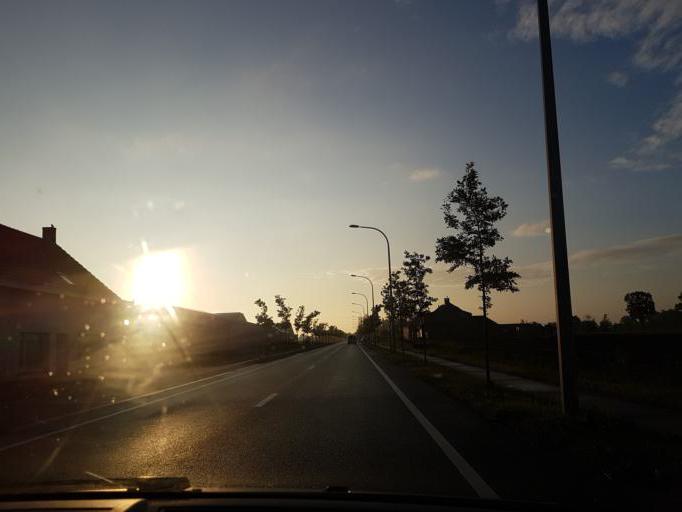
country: BE
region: Flanders
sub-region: Provincie Antwerpen
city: Hoogstraten
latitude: 51.3936
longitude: 4.7177
